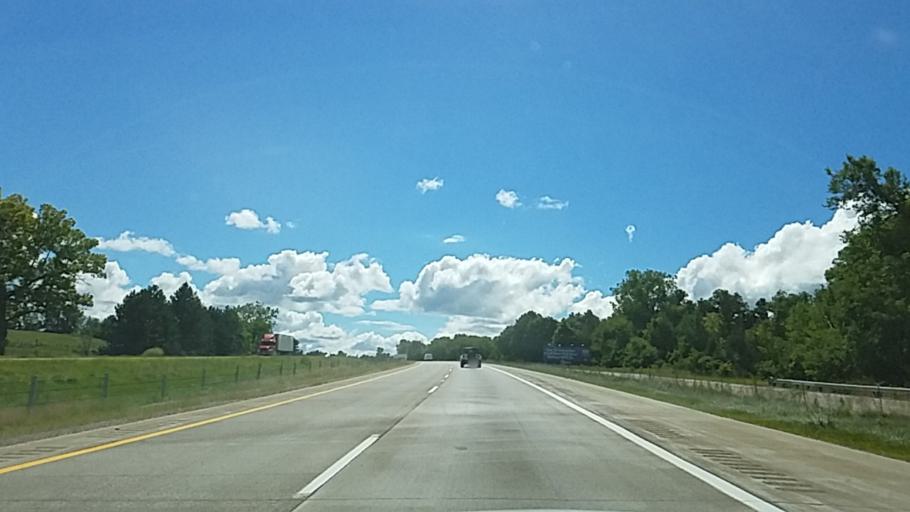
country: US
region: Michigan
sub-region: Genesee County
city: Linden
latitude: 42.7525
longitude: -83.7632
